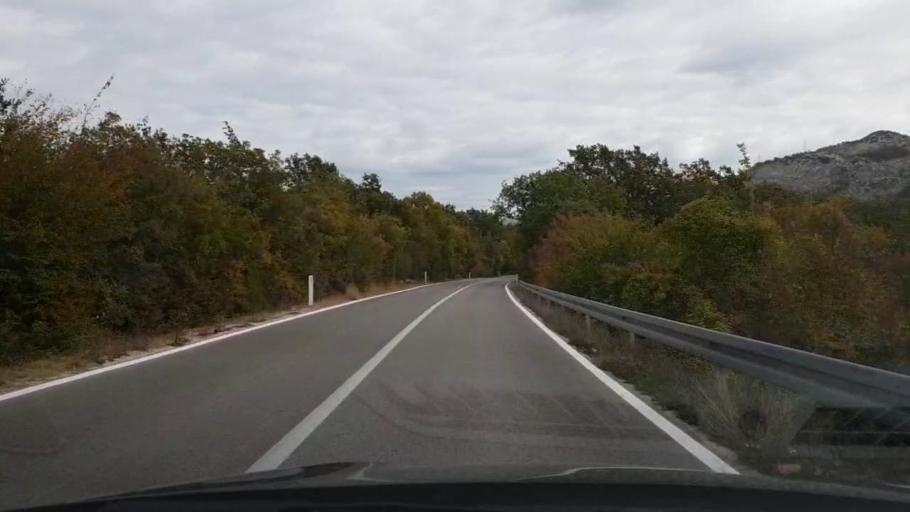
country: BA
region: Republika Srpska
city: Trebinje
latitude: 42.6873
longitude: 18.2835
